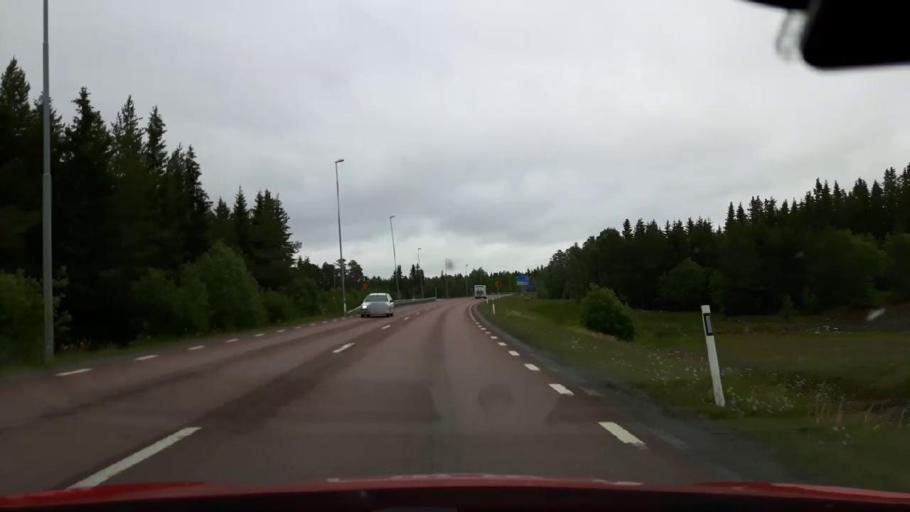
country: SE
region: Jaemtland
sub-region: OEstersunds Kommun
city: Brunflo
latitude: 63.0683
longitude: 14.8395
